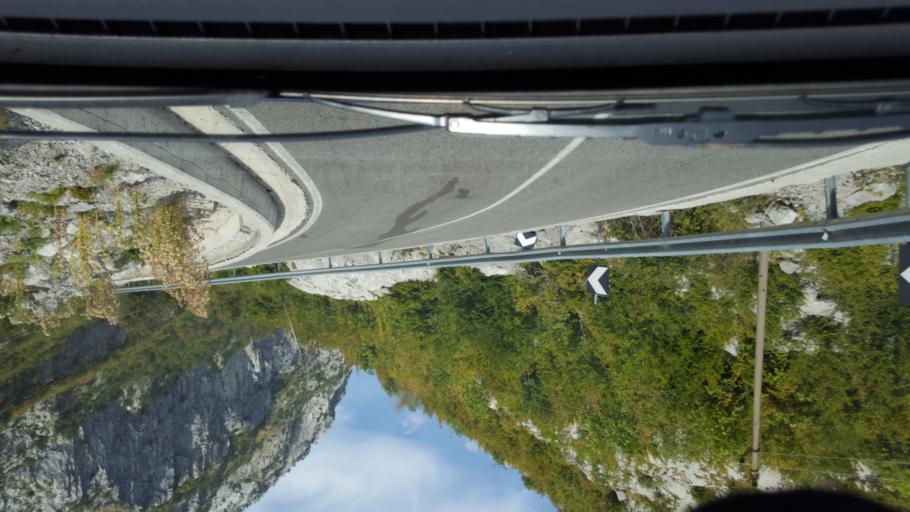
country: AL
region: Shkoder
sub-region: Rrethi i Malesia e Madhe
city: Kastrat
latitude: 42.5239
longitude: 19.6347
